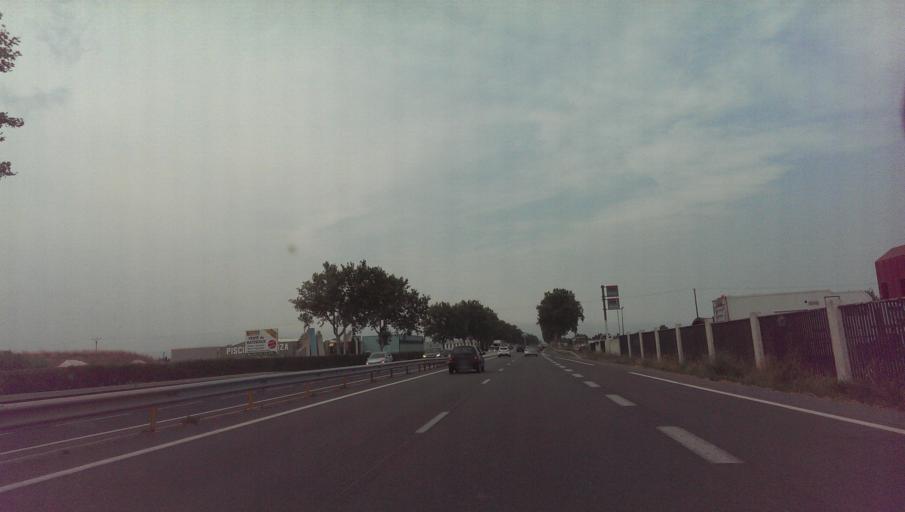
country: FR
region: Languedoc-Roussillon
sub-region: Departement des Pyrenees-Orientales
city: Pia
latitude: 42.7563
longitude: 2.8966
